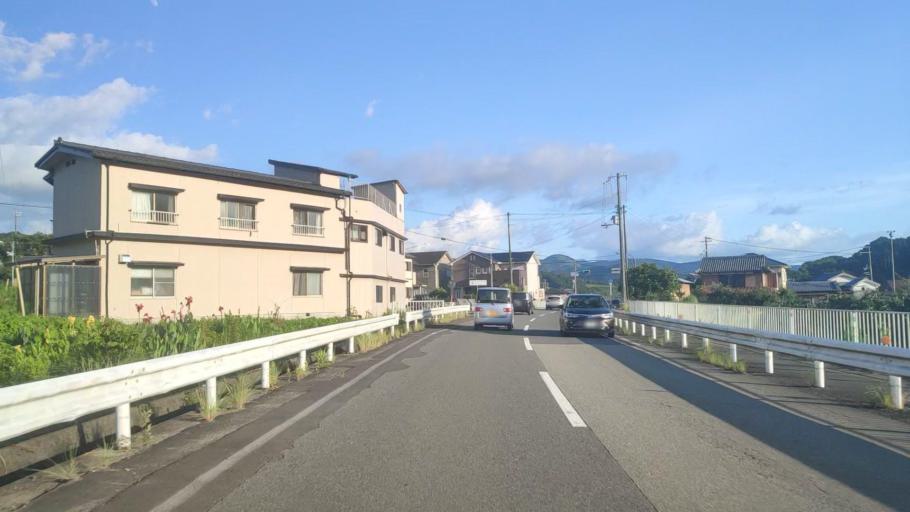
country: JP
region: Wakayama
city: Tanabe
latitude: 33.7216
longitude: 135.4456
